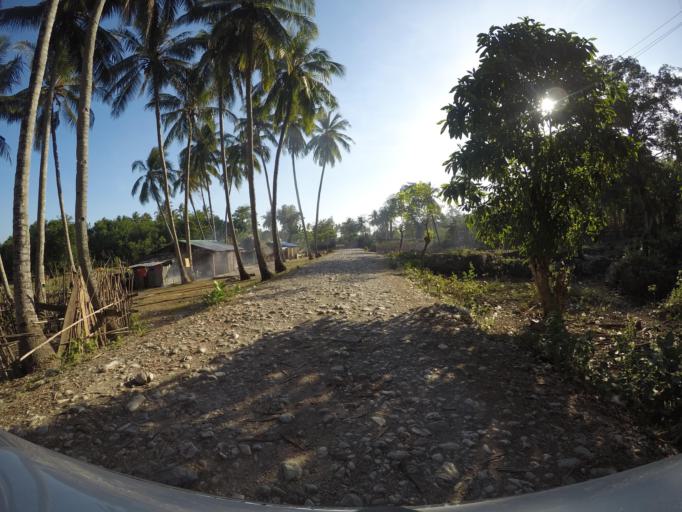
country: TL
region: Viqueque
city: Viqueque
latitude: -8.8026
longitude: 126.5845
